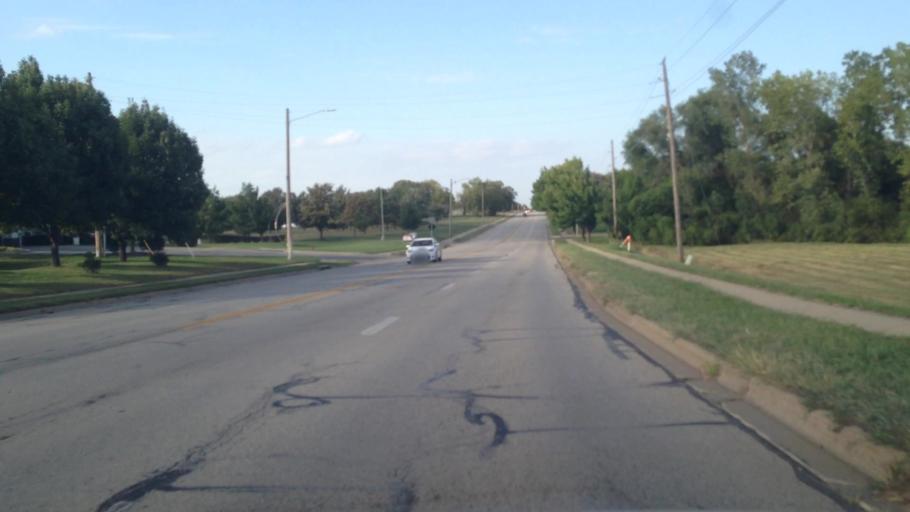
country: US
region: Kansas
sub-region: Douglas County
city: Lawrence
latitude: 38.9439
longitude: -95.3072
